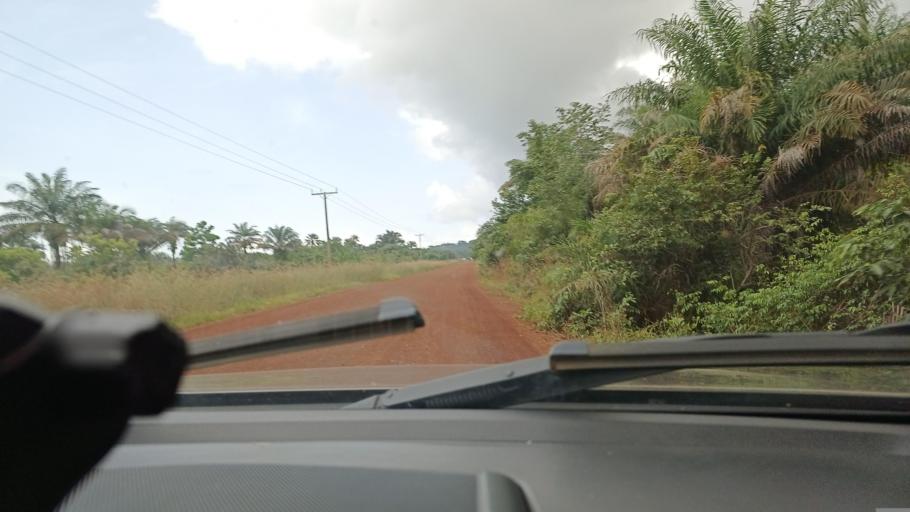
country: LR
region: Grand Cape Mount
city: Robertsport
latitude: 6.7039
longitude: -11.3242
